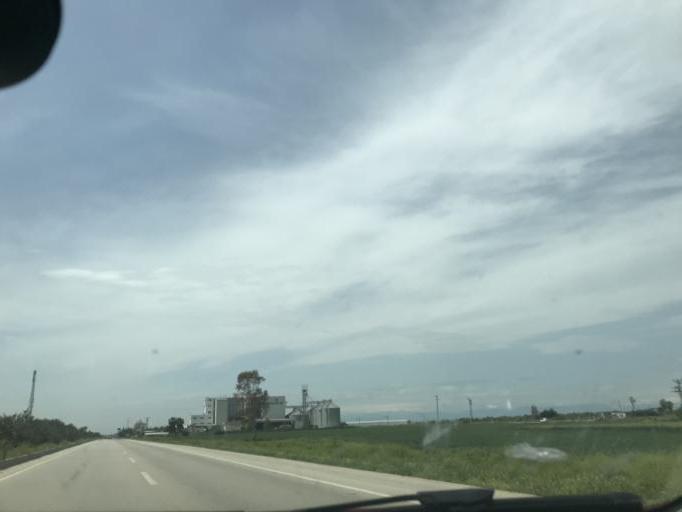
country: TR
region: Adana
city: Yakapinar
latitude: 36.9740
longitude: 35.5008
